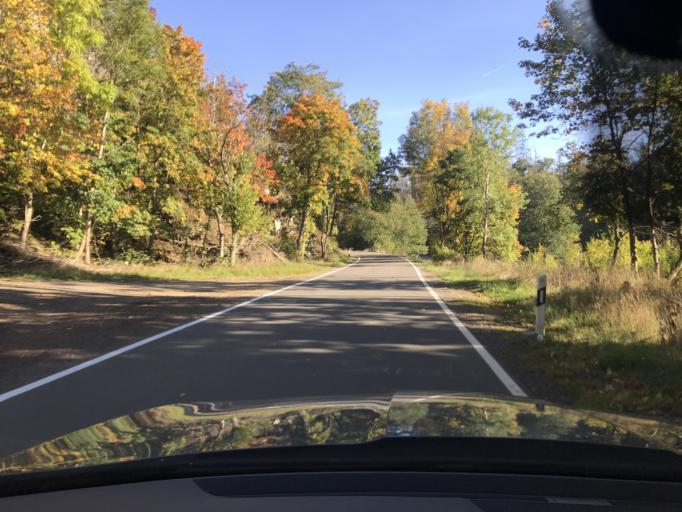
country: DE
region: Saxony-Anhalt
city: Friedrichsbrunn
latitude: 51.6884
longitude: 10.9649
